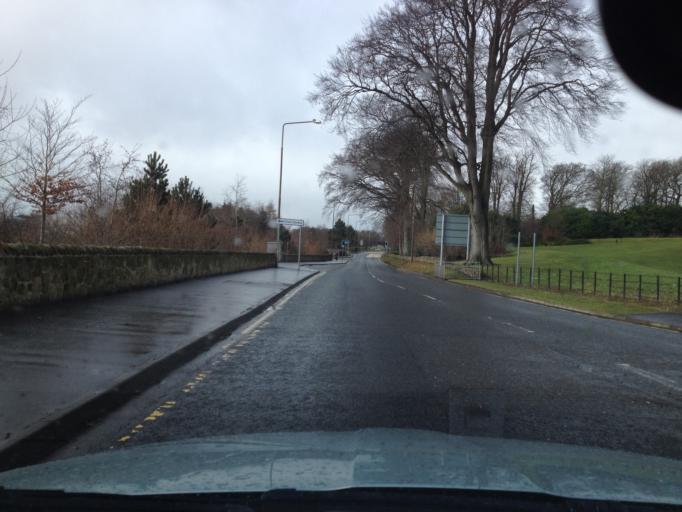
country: GB
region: Scotland
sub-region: West Lothian
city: Livingston
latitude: 55.8881
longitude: -3.5147
